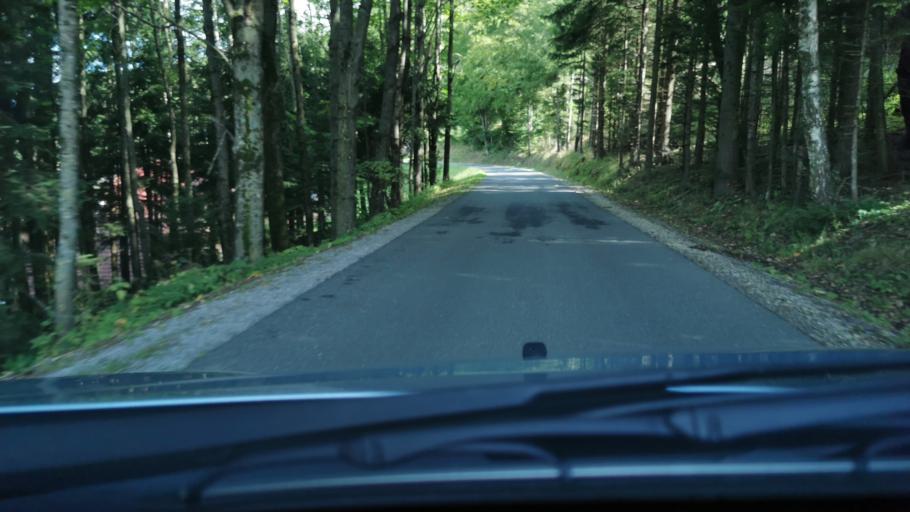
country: AT
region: Styria
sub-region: Politischer Bezirk Weiz
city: Koglhof
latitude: 47.3128
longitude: 15.7057
